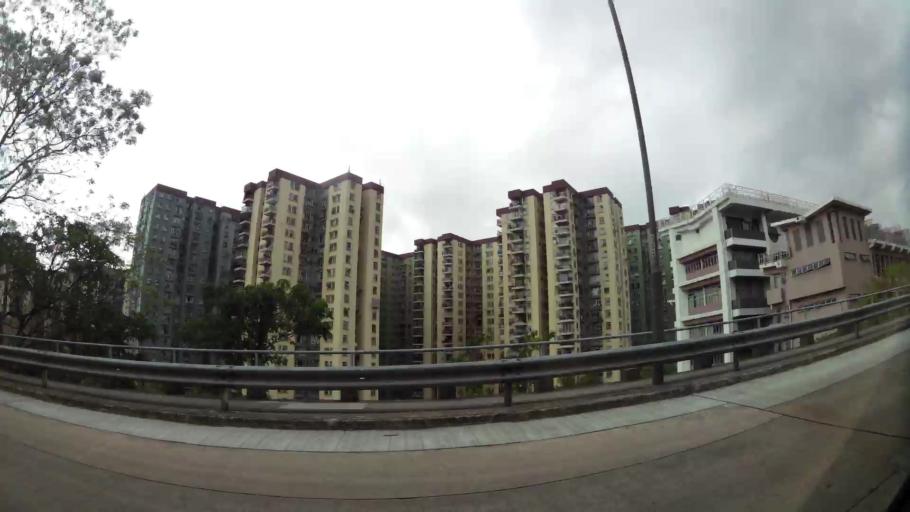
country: HK
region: Sham Shui Po
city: Sham Shui Po
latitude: 22.3385
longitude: 114.1414
